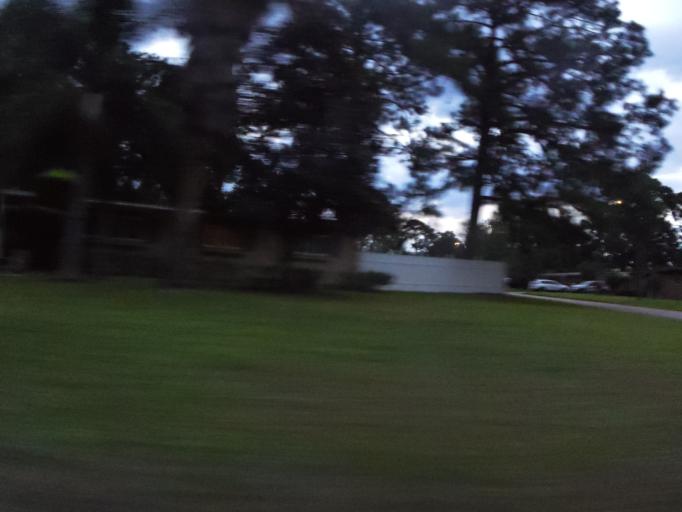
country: US
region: Florida
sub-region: Duval County
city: Jacksonville
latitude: 30.2737
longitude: -81.6188
